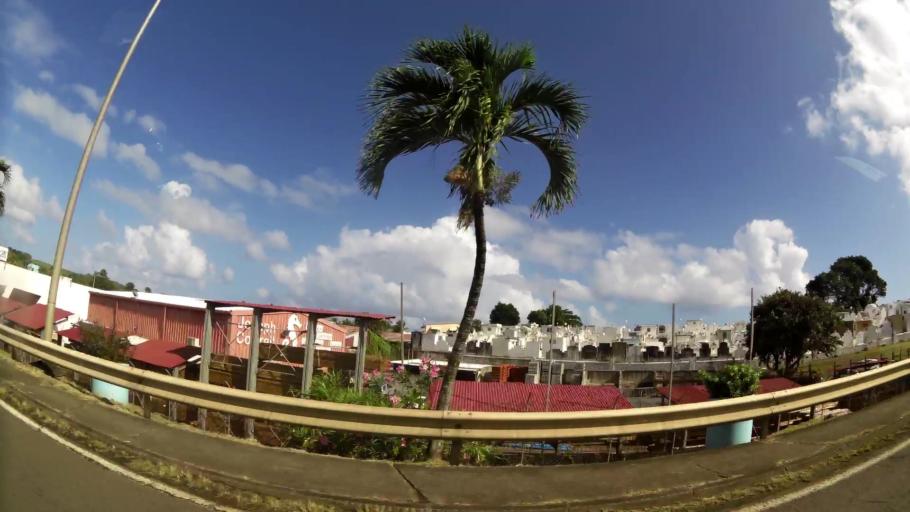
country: MQ
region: Martinique
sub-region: Martinique
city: Sainte-Marie
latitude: 14.7836
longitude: -60.9950
